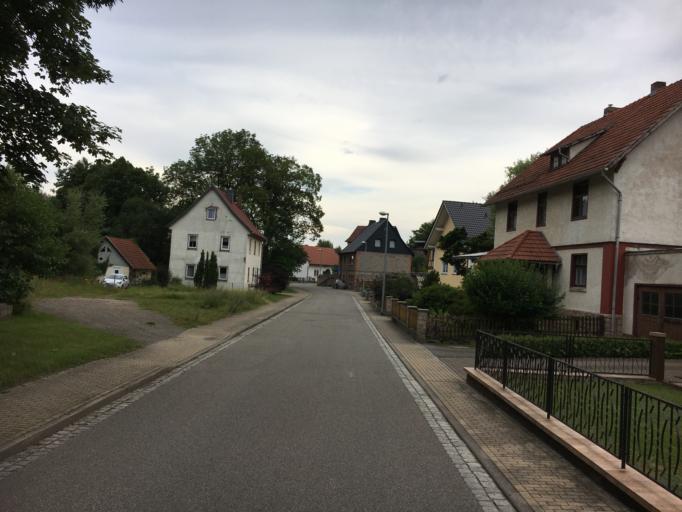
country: DE
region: Thuringia
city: Schmalkalden
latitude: 50.7552
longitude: 10.4674
